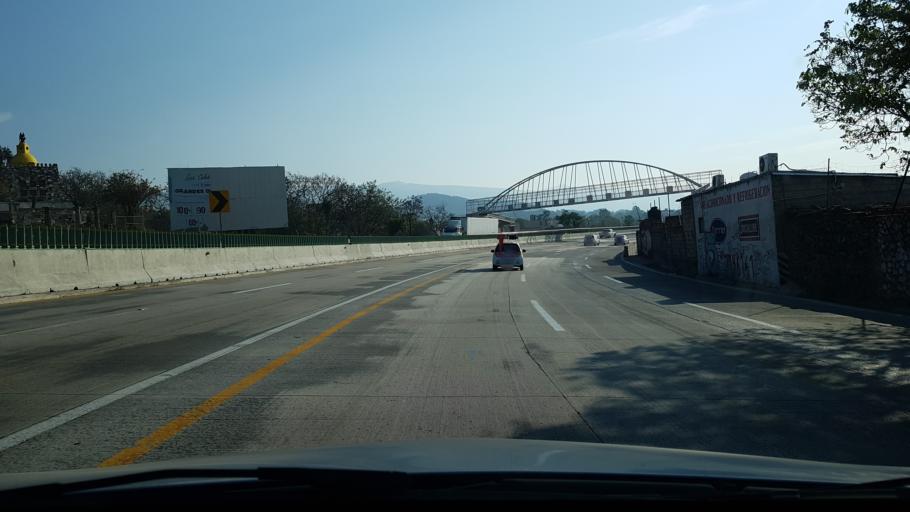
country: MX
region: Morelos
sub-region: Cuernavaca
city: Colonia los Cerritos
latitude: 18.9594
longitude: -99.2192
